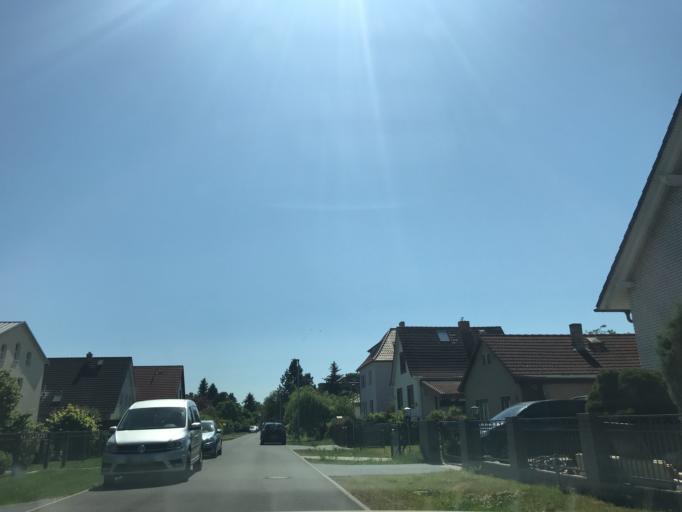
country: DE
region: Brandenburg
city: Falkensee
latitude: 52.5547
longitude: 13.0781
